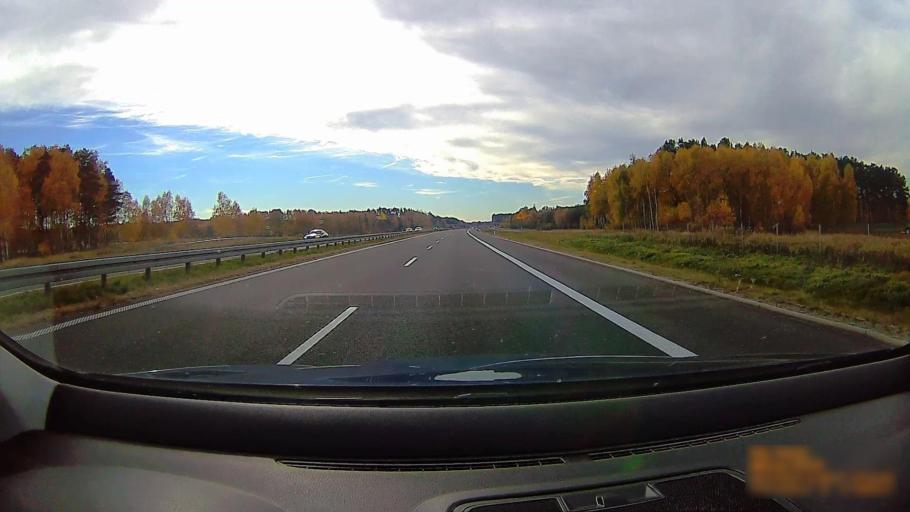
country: PL
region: Greater Poland Voivodeship
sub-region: Powiat ostrowski
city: Przygodzice
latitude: 51.5730
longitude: 17.8487
